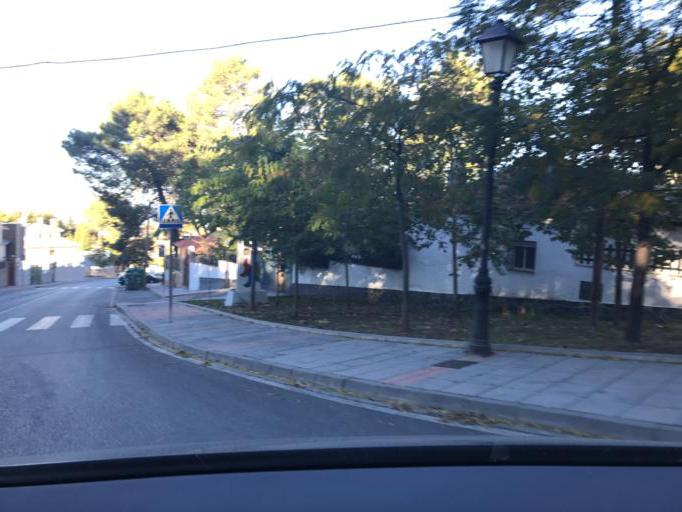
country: ES
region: Andalusia
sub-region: Provincia de Granada
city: Viznar
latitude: 37.2455
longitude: -3.5535
